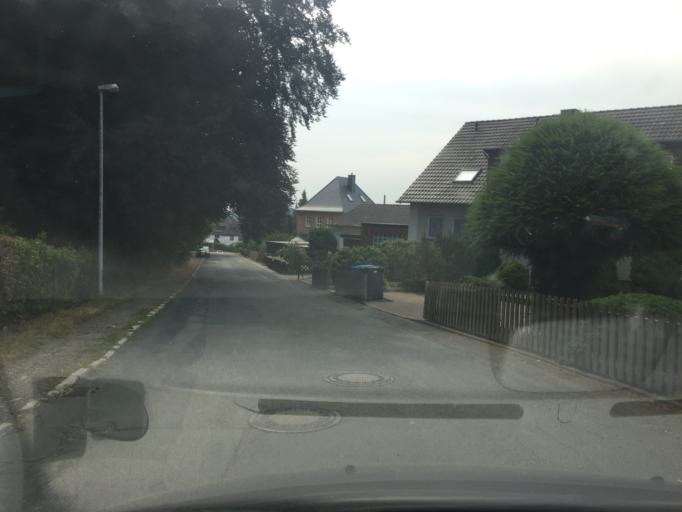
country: DE
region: Lower Saxony
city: Bad Sachsa
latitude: 51.5982
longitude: 10.5555
